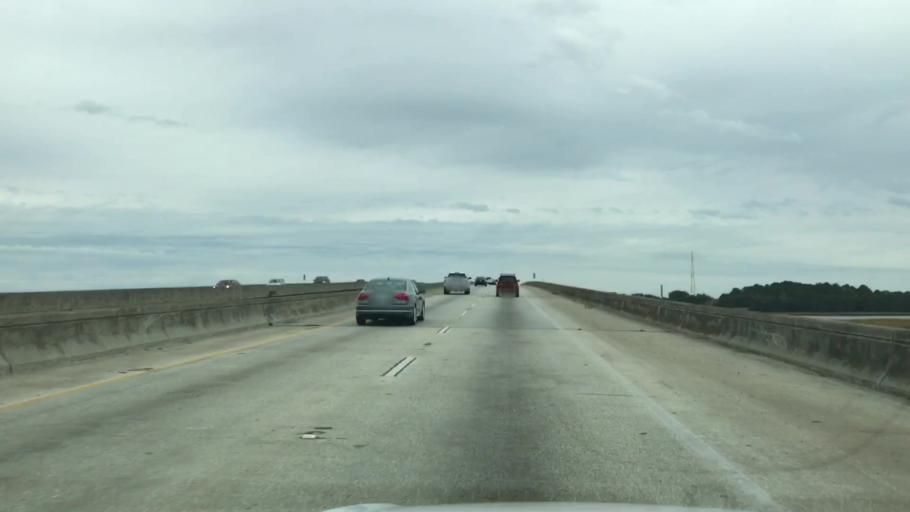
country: US
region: South Carolina
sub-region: Charleston County
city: North Charleston
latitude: 32.8320
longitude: -80.0274
